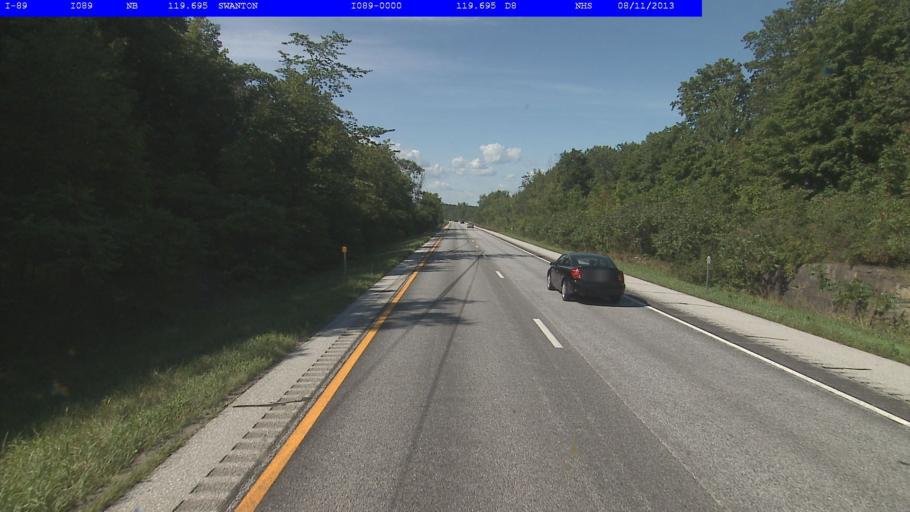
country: US
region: Vermont
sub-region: Franklin County
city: Saint Albans
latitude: 44.8727
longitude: -73.0822
